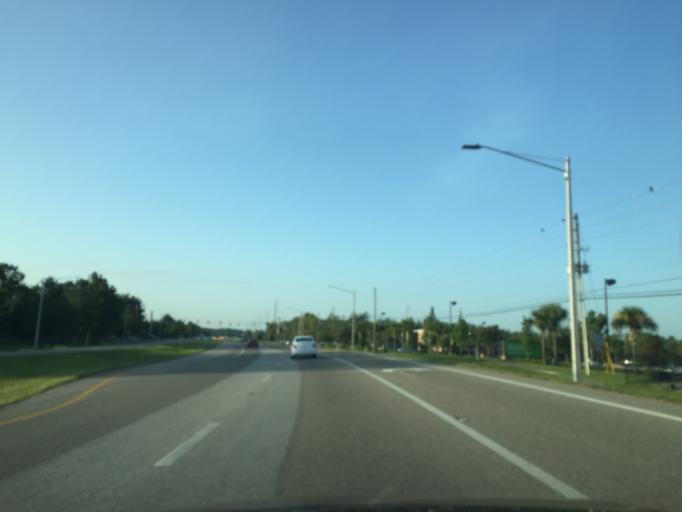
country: US
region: Florida
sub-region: Orange County
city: Alafaya
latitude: 28.5373
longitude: -81.2080
